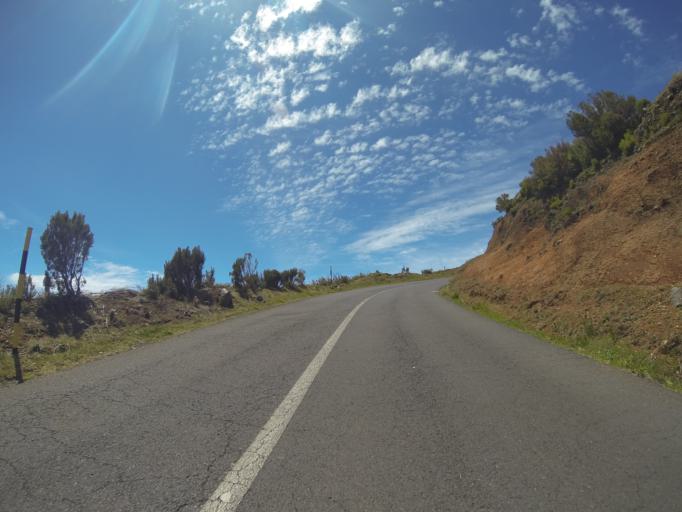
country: PT
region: Madeira
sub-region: Funchal
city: Nossa Senhora do Monte
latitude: 32.7181
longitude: -16.9058
